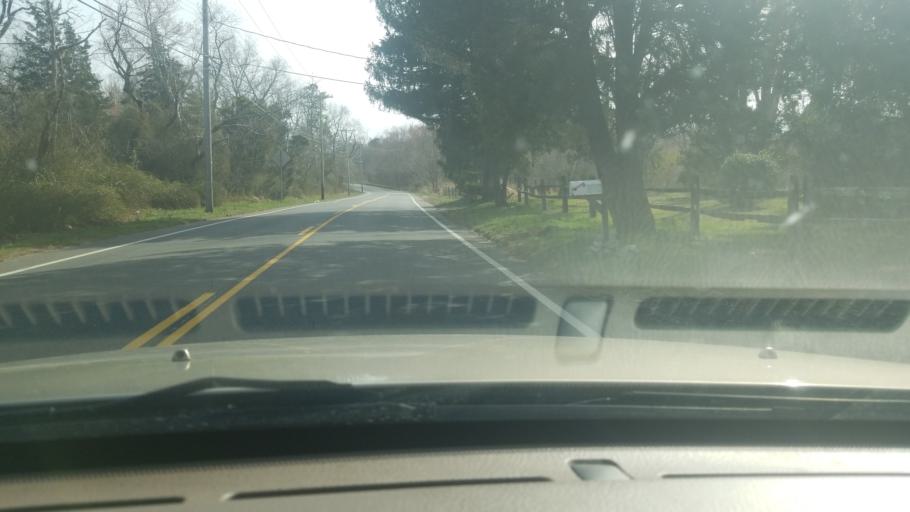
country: US
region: New Jersey
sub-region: Ocean County
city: Cedar Glen West
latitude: 40.0639
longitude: -74.2736
